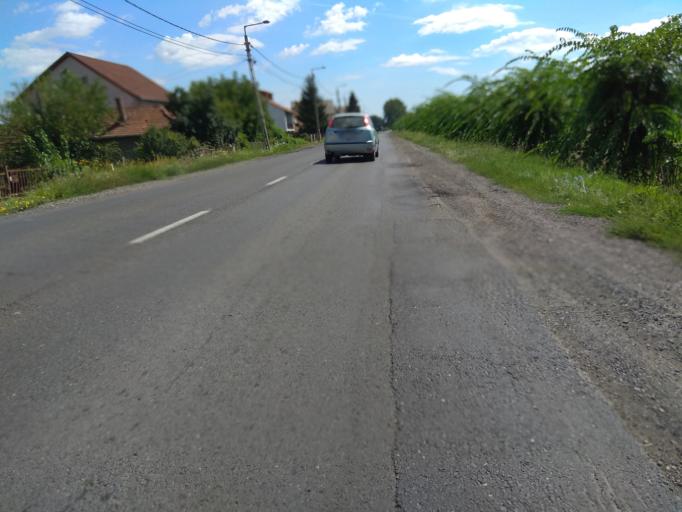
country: HU
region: Borsod-Abauj-Zemplen
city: Sajokaza
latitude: 48.2715
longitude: 20.5832
